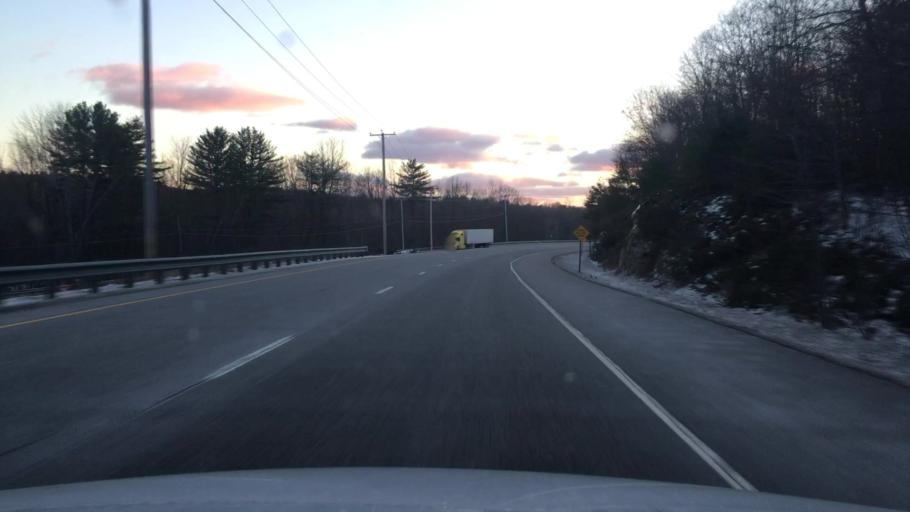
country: US
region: Maine
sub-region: Androscoggin County
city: Auburn
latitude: 44.0496
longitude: -70.2561
